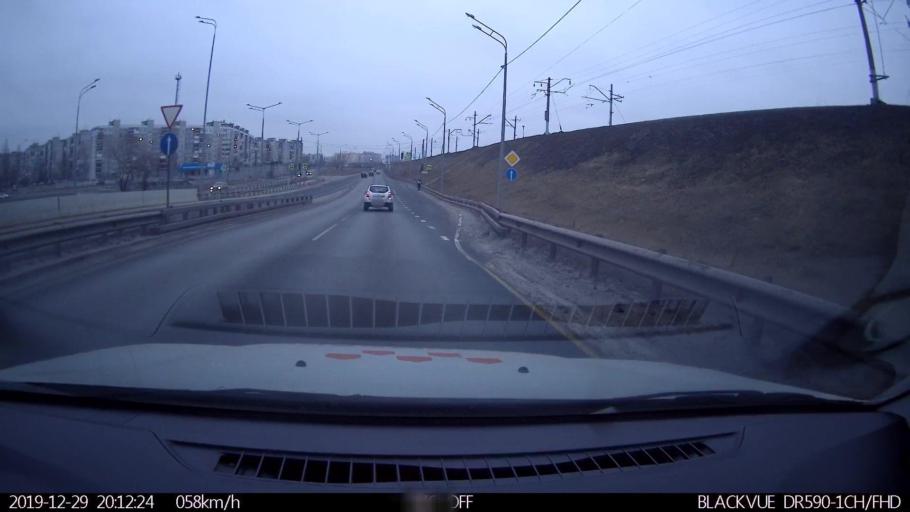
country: RU
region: Nizjnij Novgorod
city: Nizhniy Novgorod
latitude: 56.3469
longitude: 43.9213
